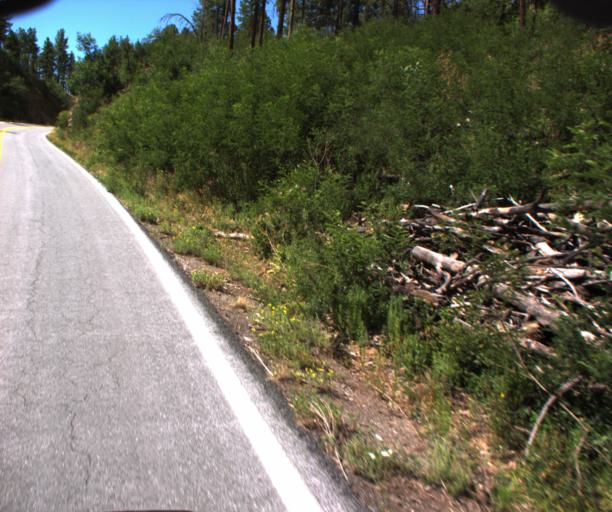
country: US
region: Arizona
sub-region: Apache County
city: Eagar
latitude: 33.7719
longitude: -109.1885
